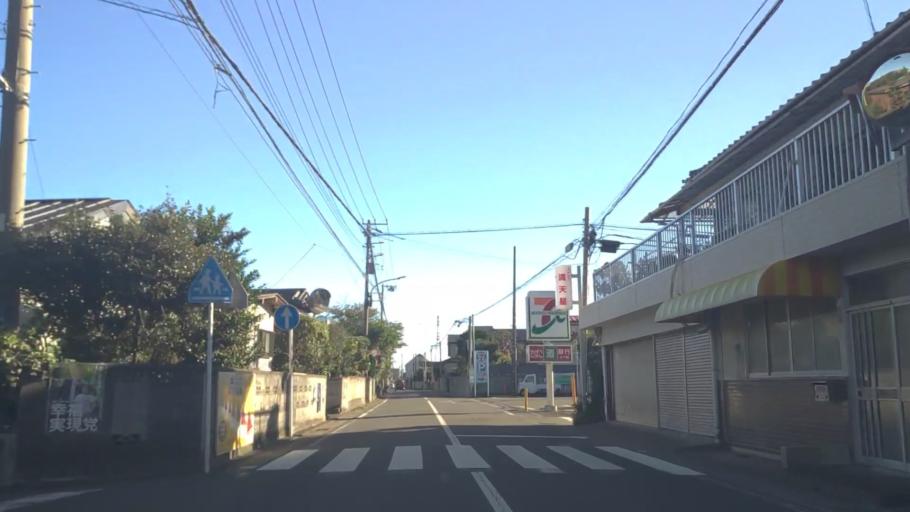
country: JP
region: Kanagawa
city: Isehara
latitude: 35.3776
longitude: 139.3649
